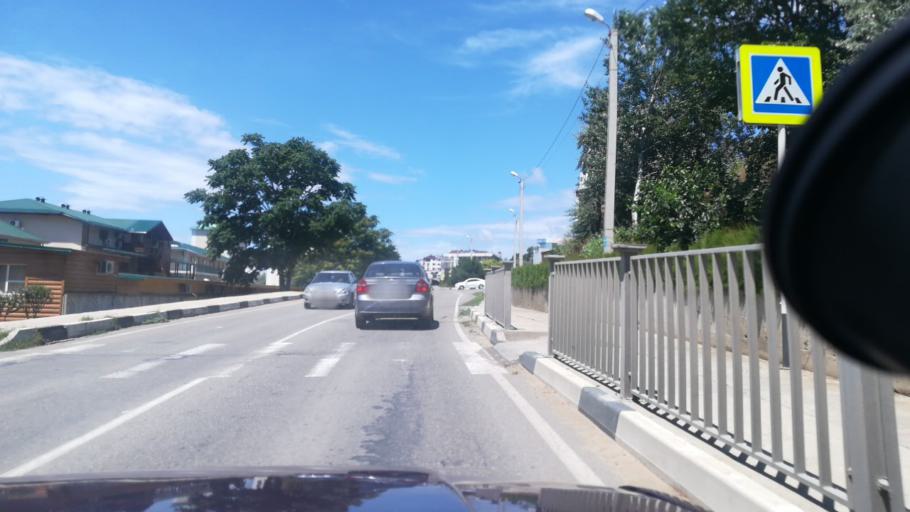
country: RU
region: Krasnodarskiy
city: Vityazevo
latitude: 44.9770
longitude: 37.2728
